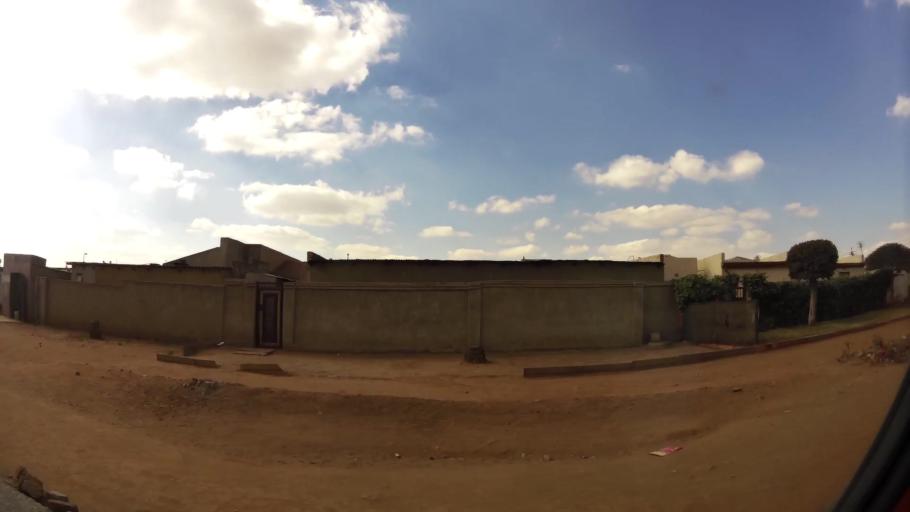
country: ZA
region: Gauteng
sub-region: Ekurhuleni Metropolitan Municipality
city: Tembisa
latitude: -25.9966
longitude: 28.2050
